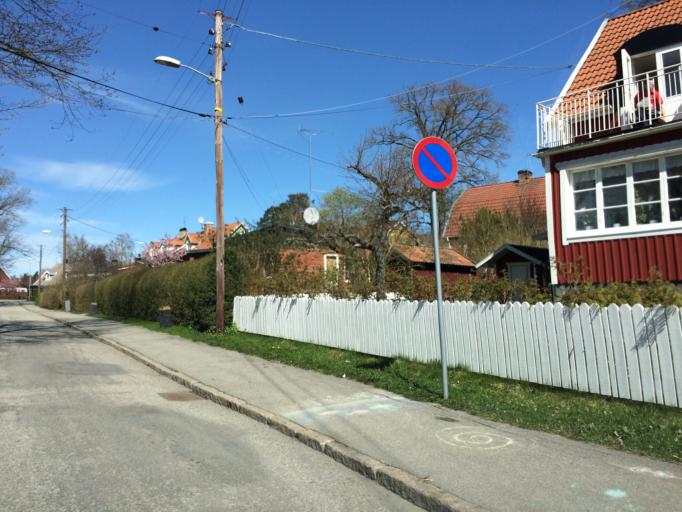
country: SE
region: Stockholm
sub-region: Huddinge Kommun
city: Huddinge
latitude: 59.2771
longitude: 17.9846
